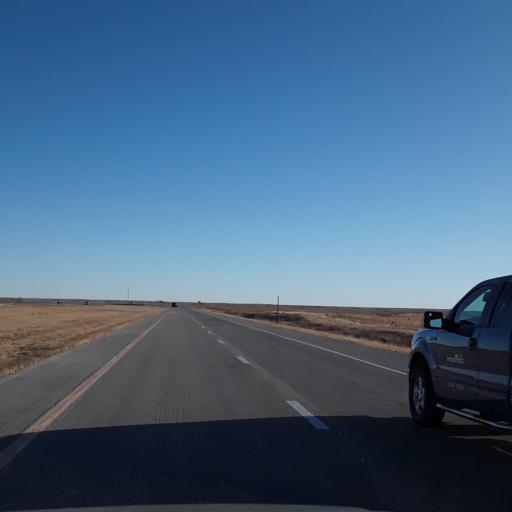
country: US
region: Kansas
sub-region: Seward County
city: Liberal
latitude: 37.1107
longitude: -100.7819
